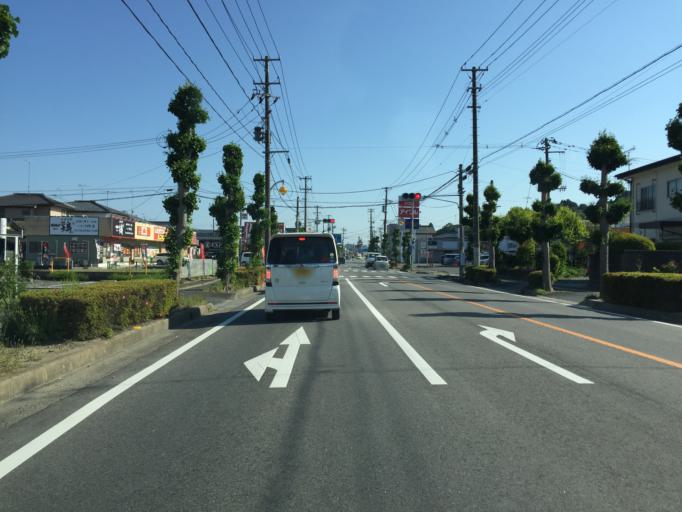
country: JP
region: Ibaraki
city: Kitaibaraki
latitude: 36.9143
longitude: 140.7748
